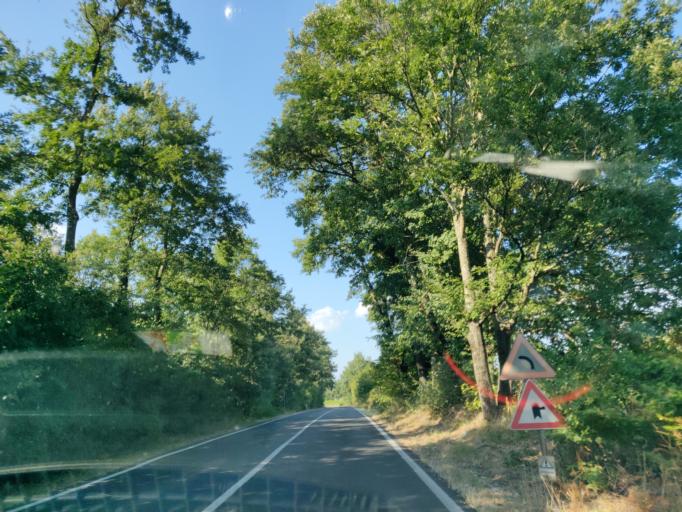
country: IT
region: Latium
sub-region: Provincia di Viterbo
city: Latera
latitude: 42.6038
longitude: 11.8430
